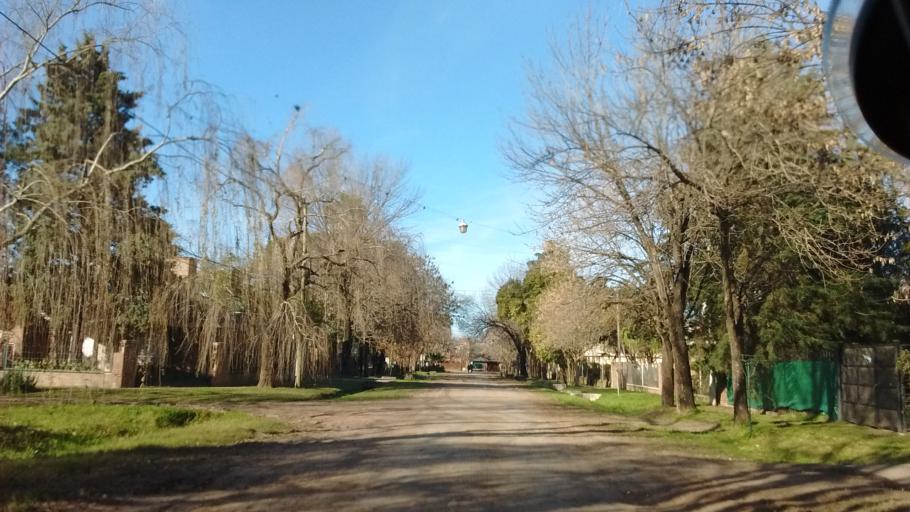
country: AR
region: Santa Fe
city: Funes
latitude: -32.9282
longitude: -60.8066
